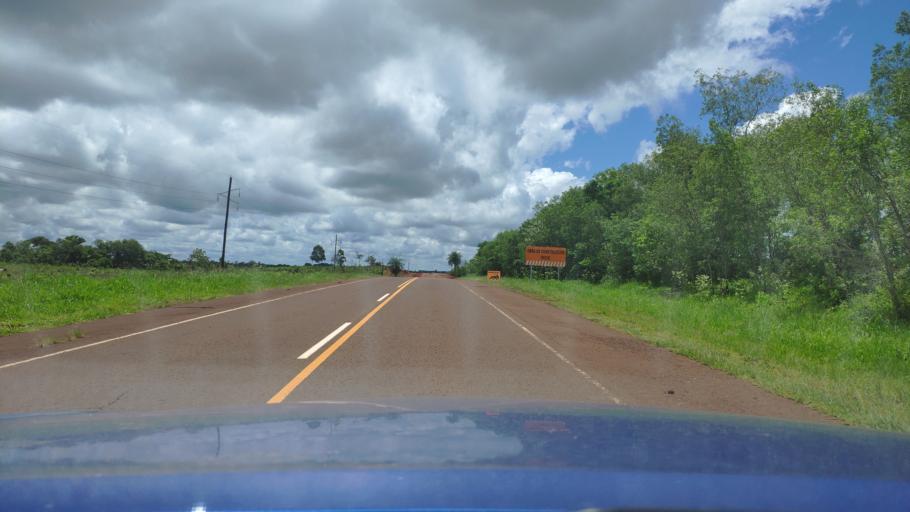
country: AR
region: Misiones
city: Picada Gobernador Lopez
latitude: -27.6725
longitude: -55.2797
